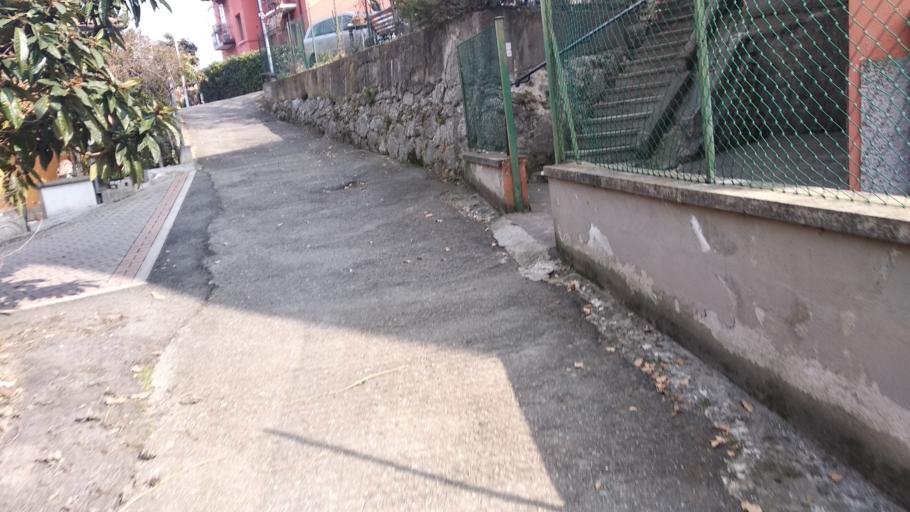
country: IT
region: Emilia-Romagna
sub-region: Provincia di Bologna
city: Ponticella
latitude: 44.4583
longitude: 11.3746
